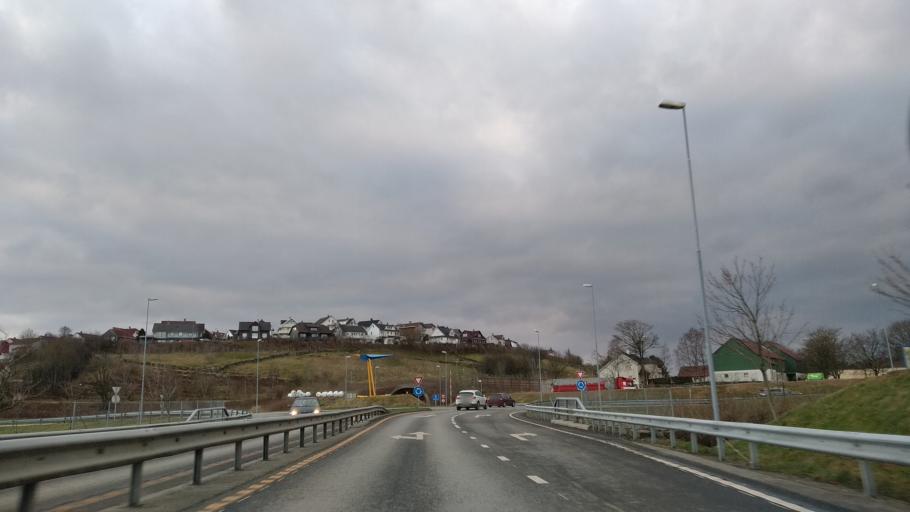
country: NO
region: Rogaland
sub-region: Klepp
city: Kleppe
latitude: 58.7795
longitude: 5.6244
